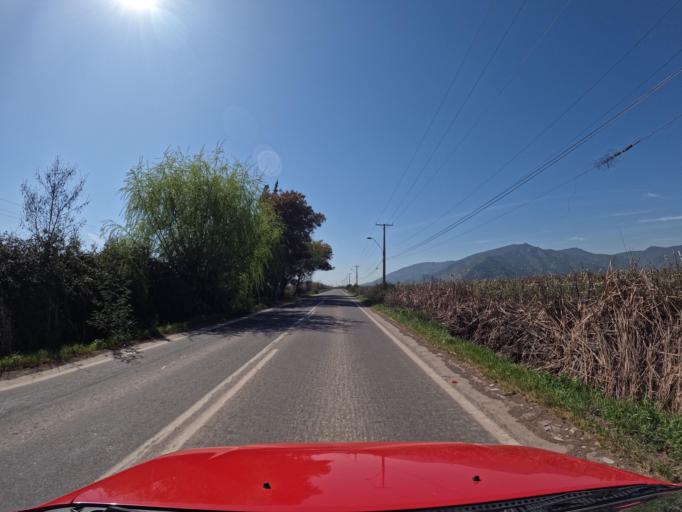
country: CL
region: Maule
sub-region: Provincia de Curico
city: Rauco
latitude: -35.0329
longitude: -71.4440
